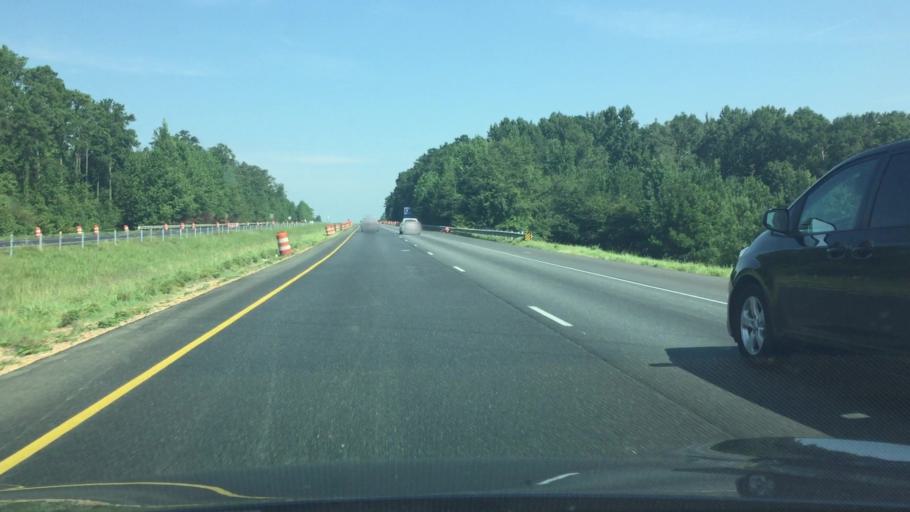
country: US
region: Alabama
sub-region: Autauga County
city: Marbury
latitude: 32.7277
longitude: -86.5366
